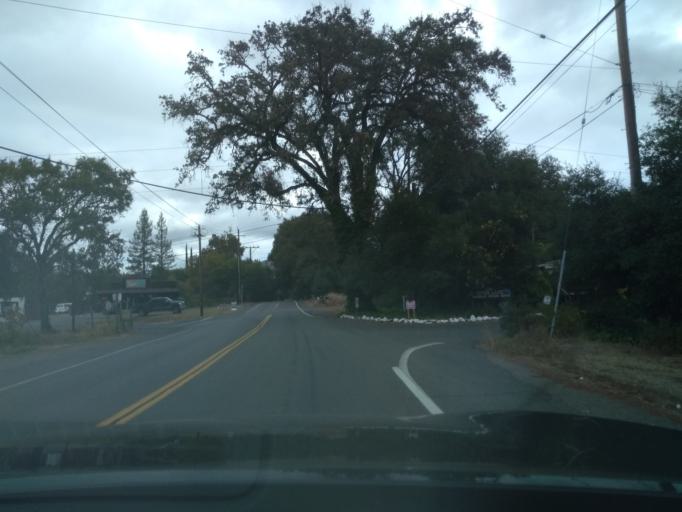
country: US
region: California
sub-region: Mendocino County
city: Ukiah
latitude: 39.1959
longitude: -123.1933
